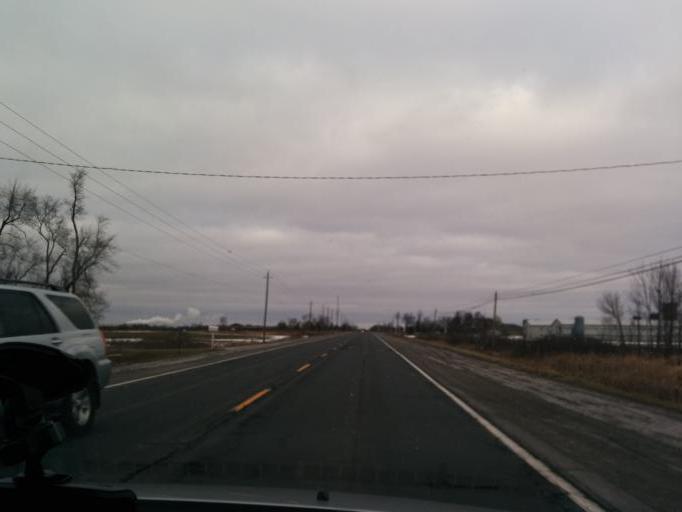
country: CA
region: Ontario
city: Ancaster
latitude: 42.9985
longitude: -80.0188
